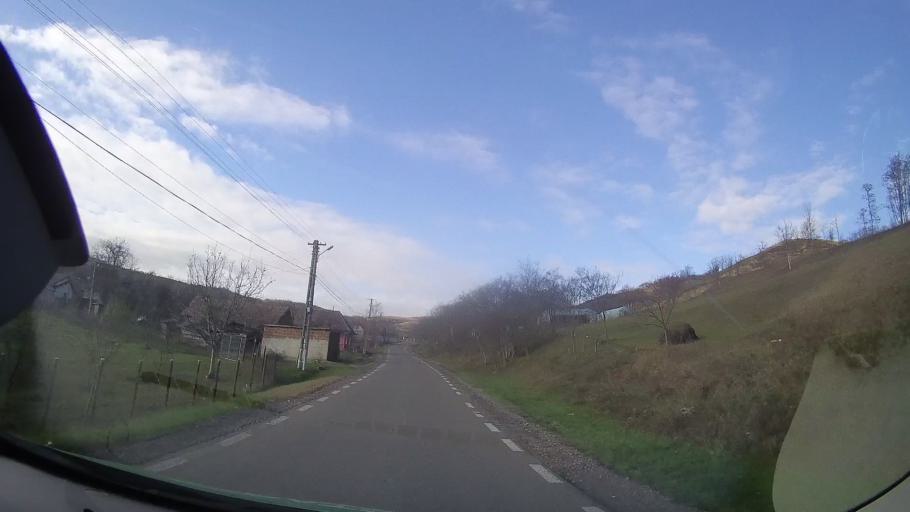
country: RO
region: Mures
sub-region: Comuna Papiu Ilarian
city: Papiu Ilarian
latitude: 46.5581
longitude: 24.1903
